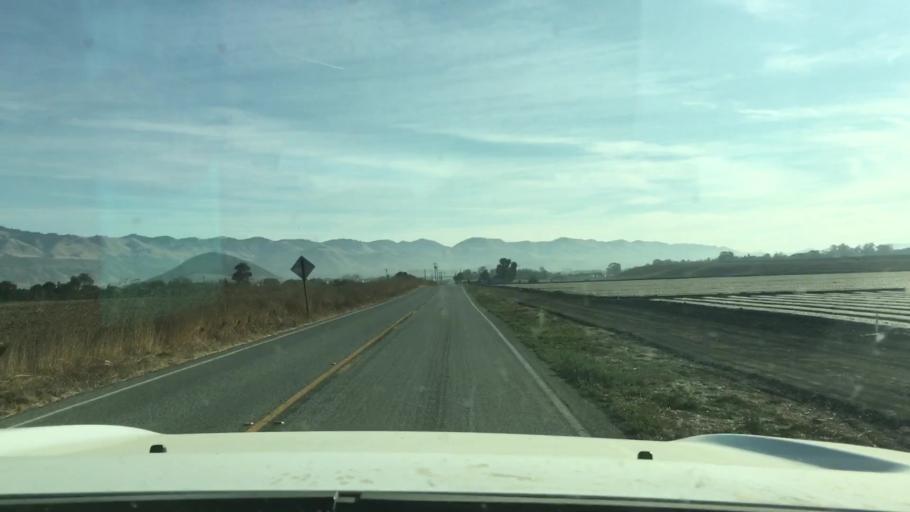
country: US
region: California
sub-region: San Luis Obispo County
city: San Luis Obispo
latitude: 35.2358
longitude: -120.6656
